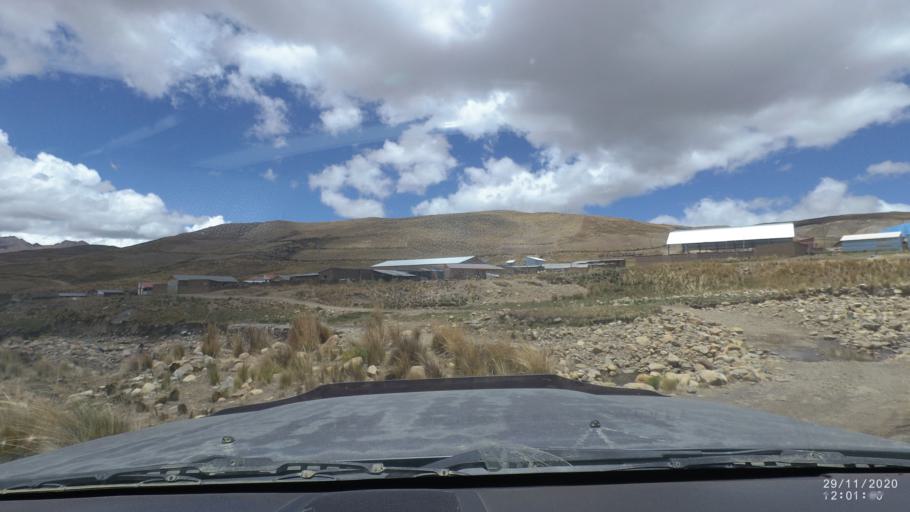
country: BO
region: Cochabamba
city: Cochabamba
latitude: -17.1509
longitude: -66.2816
